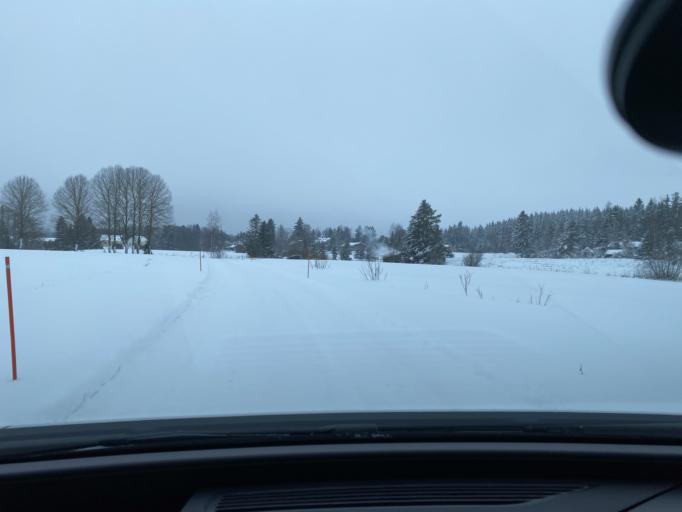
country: FI
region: Pirkanmaa
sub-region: Lounais-Pirkanmaa
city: Punkalaidun
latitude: 61.1265
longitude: 23.0836
